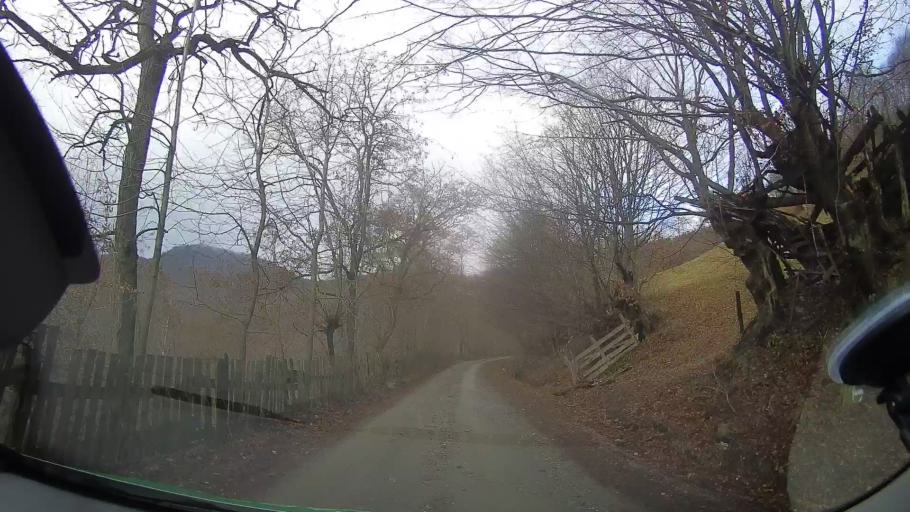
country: RO
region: Cluj
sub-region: Comuna Valea Ierii
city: Valea Ierii
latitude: 46.6469
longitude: 23.3502
